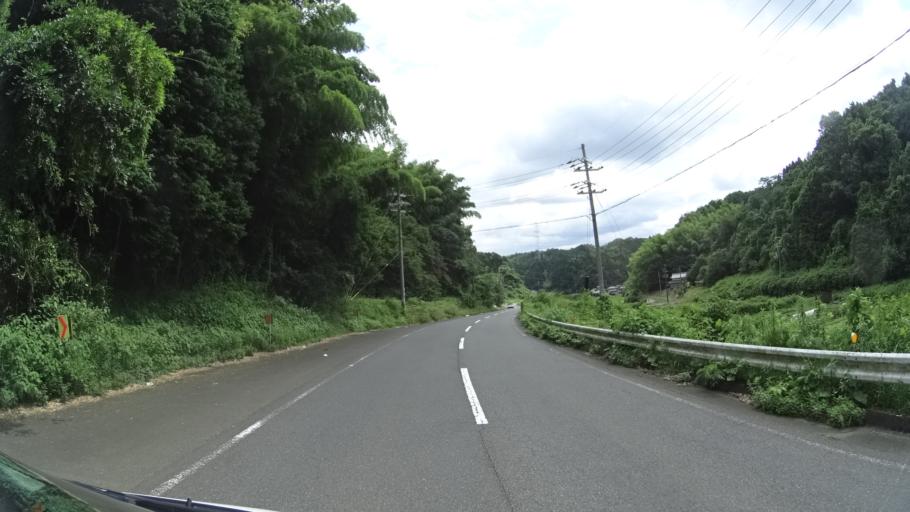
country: JP
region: Kyoto
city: Ayabe
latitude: 35.3485
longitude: 135.2741
